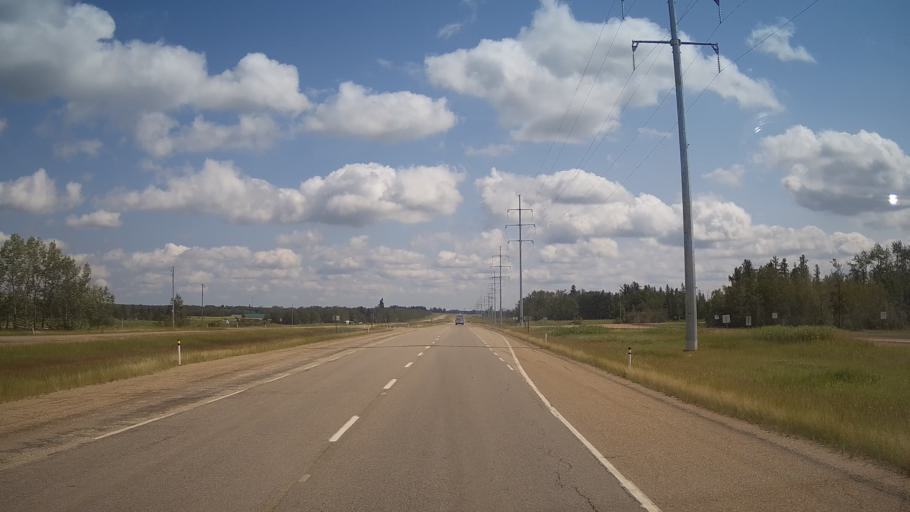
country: CA
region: Alberta
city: Sherwood Park
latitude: 53.4425
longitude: -113.2240
